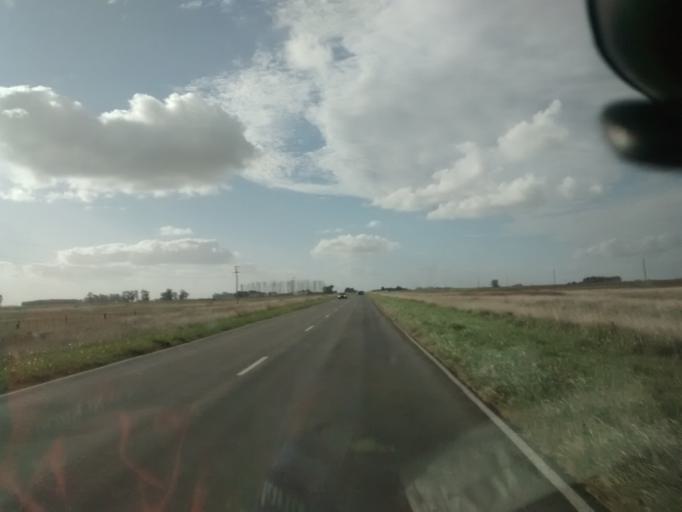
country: AR
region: Buenos Aires
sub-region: Partido de Ayacucho
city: Ayacucho
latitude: -36.9041
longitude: -58.5287
